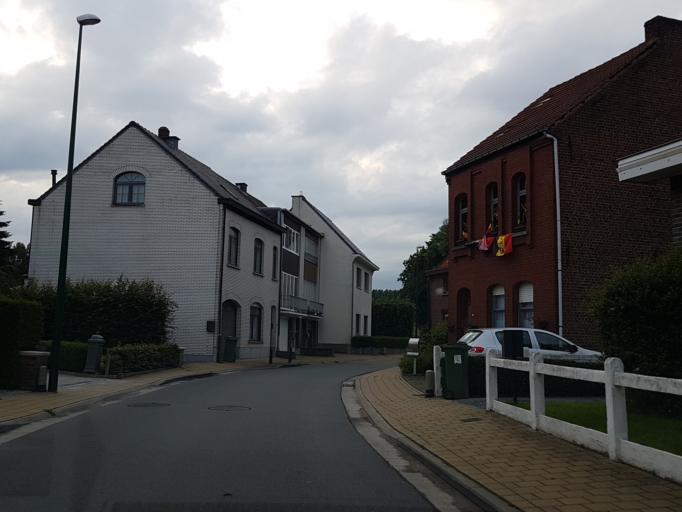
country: BE
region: Flanders
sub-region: Provincie Oost-Vlaanderen
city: Denderleeuw
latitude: 50.9057
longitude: 4.0745
